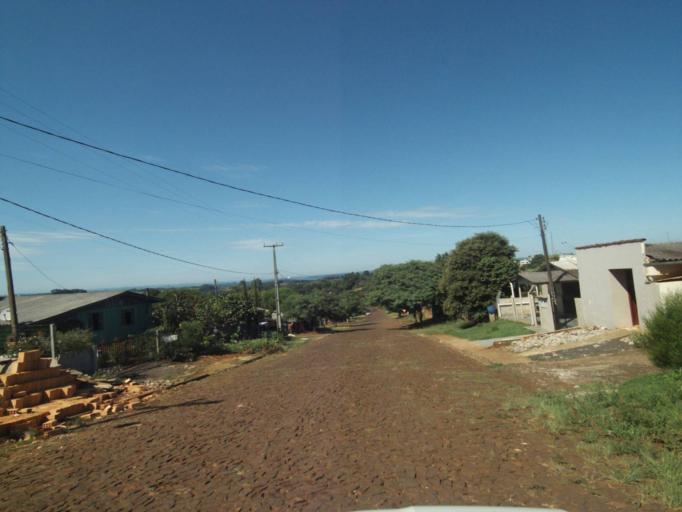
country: BR
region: Parana
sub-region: Laranjeiras Do Sul
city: Laranjeiras do Sul
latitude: -25.4935
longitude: -52.5257
